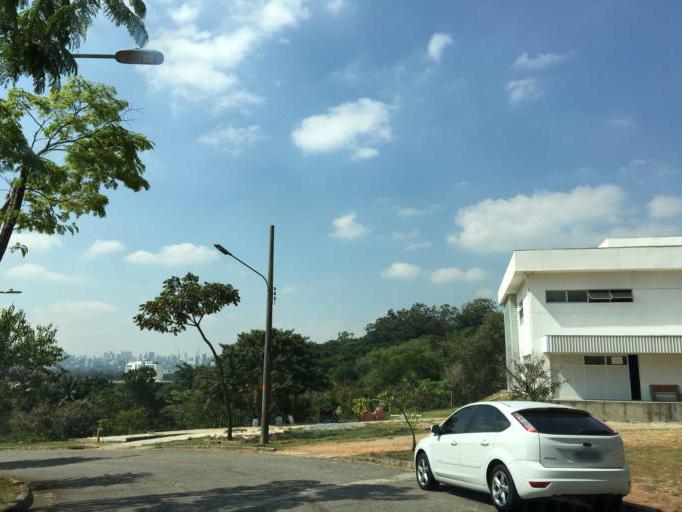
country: BR
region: Sao Paulo
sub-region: Osasco
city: Osasco
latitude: -23.5620
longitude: -46.7334
